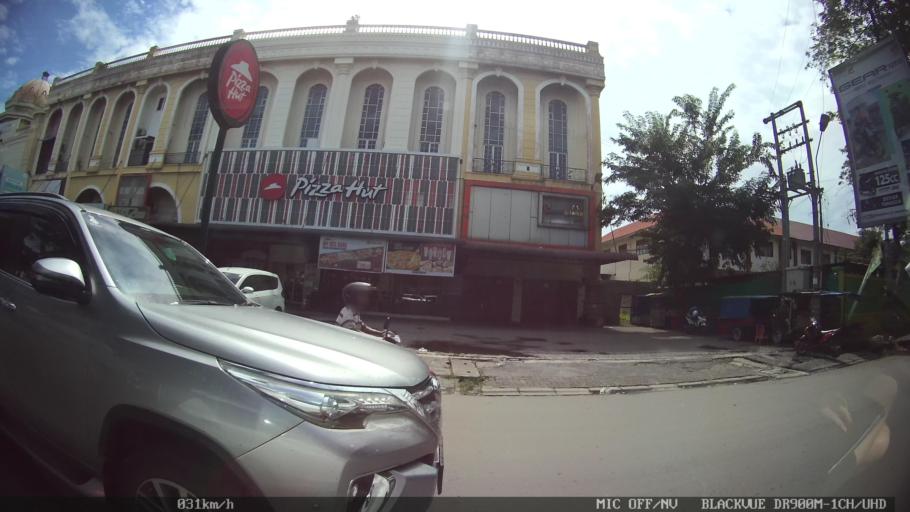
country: ID
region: North Sumatra
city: Medan
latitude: 3.6026
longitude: 98.7069
